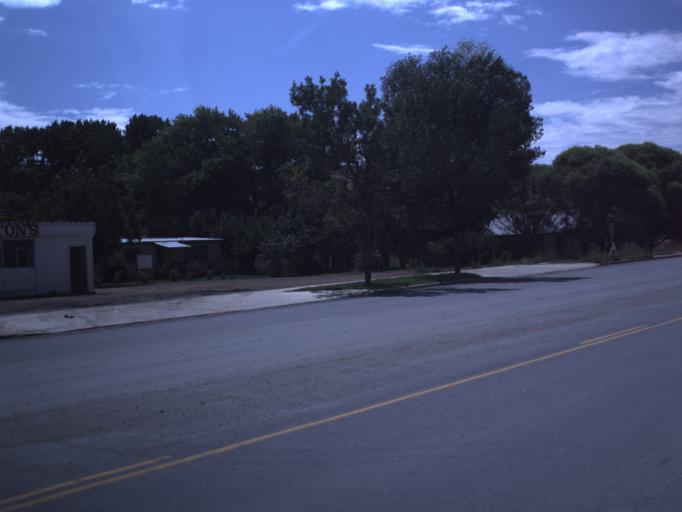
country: US
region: Utah
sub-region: Duchesne County
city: Duchesne
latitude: 40.1635
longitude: -110.4109
